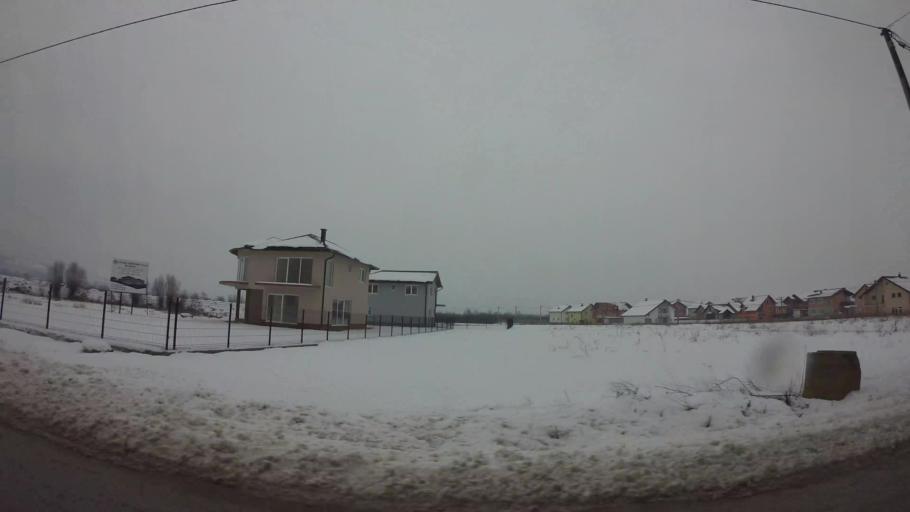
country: BA
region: Federation of Bosnia and Herzegovina
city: Hadzici
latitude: 43.8577
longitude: 18.2726
